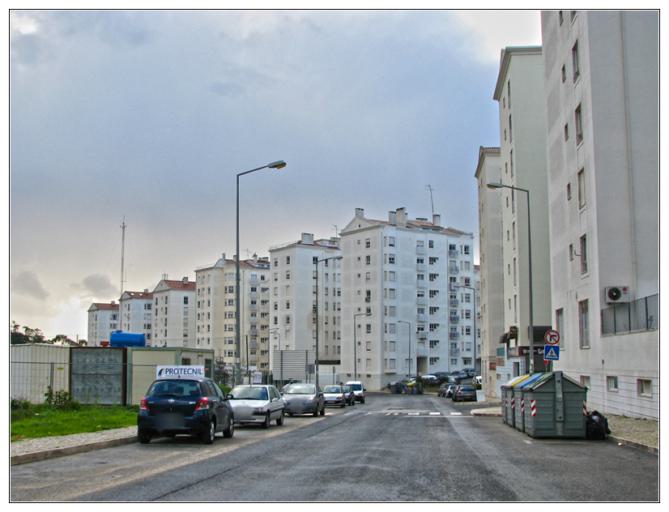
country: PT
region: Lisbon
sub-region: Sintra
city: Rio de Mouro
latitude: 38.7820
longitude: -9.3209
